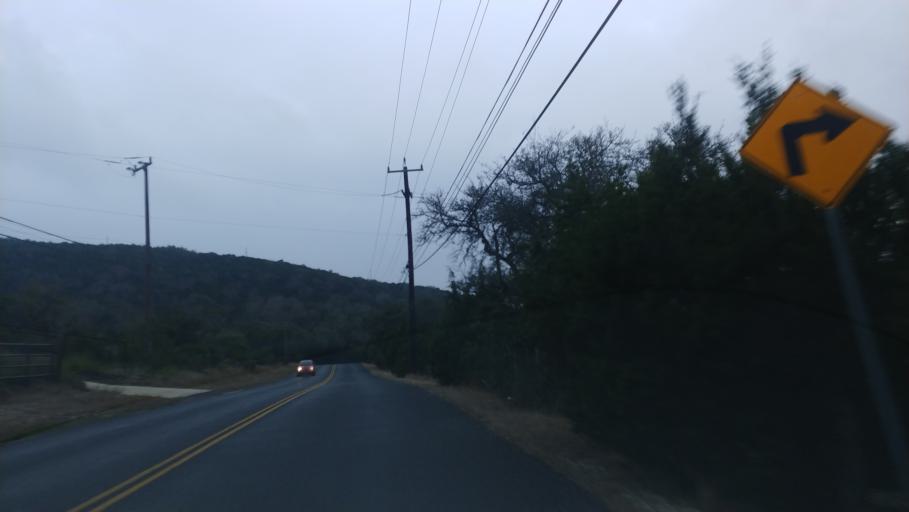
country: US
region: Texas
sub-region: Bexar County
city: Cross Mountain
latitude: 29.6368
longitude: -98.6784
